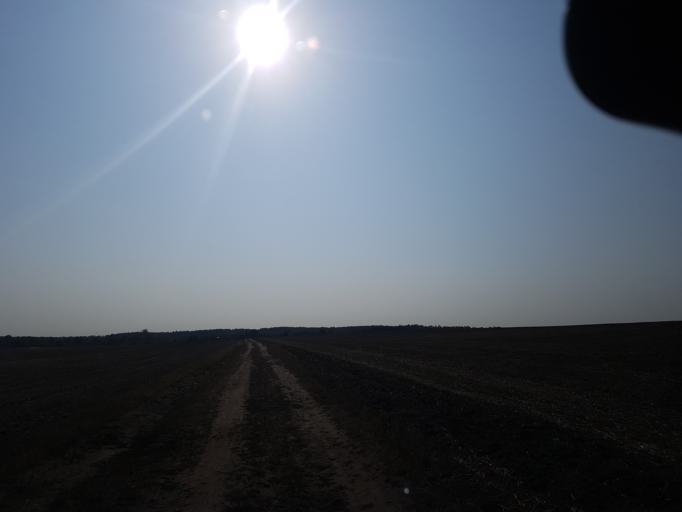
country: DE
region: Brandenburg
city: Wiesenburg
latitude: 52.0618
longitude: 12.3705
